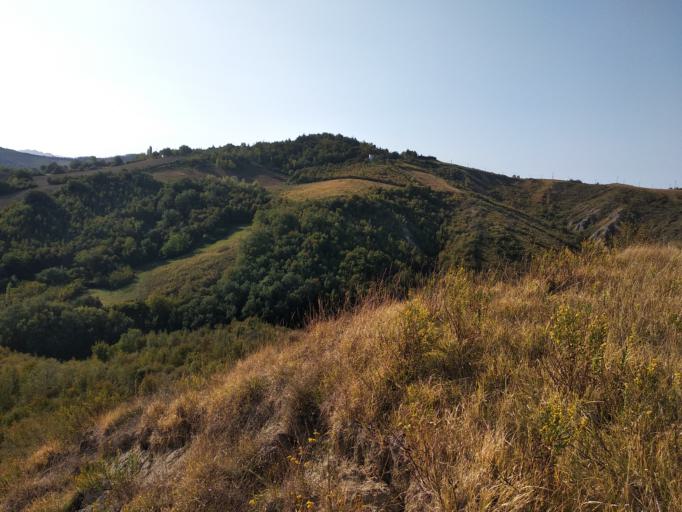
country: IT
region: Emilia-Romagna
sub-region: Provincia di Bologna
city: Borgo Tossignano
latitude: 44.3292
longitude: 11.5640
